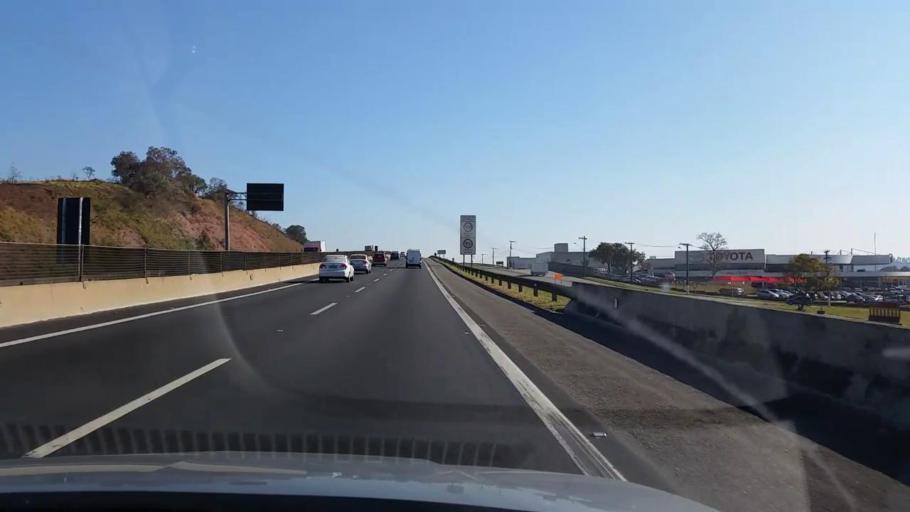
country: BR
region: Sao Paulo
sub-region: Jundiai
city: Jundiai
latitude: -23.2286
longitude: -46.8740
